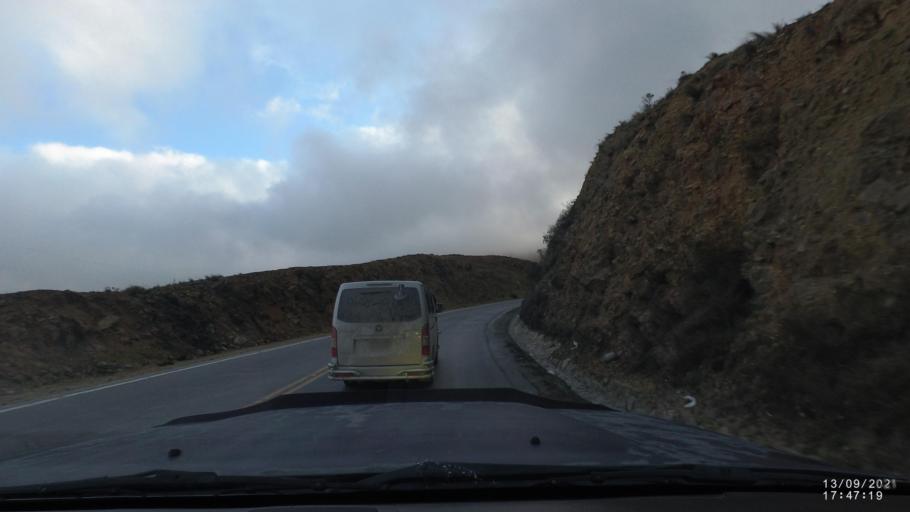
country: BO
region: Cochabamba
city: Colomi
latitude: -17.3907
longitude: -65.8320
